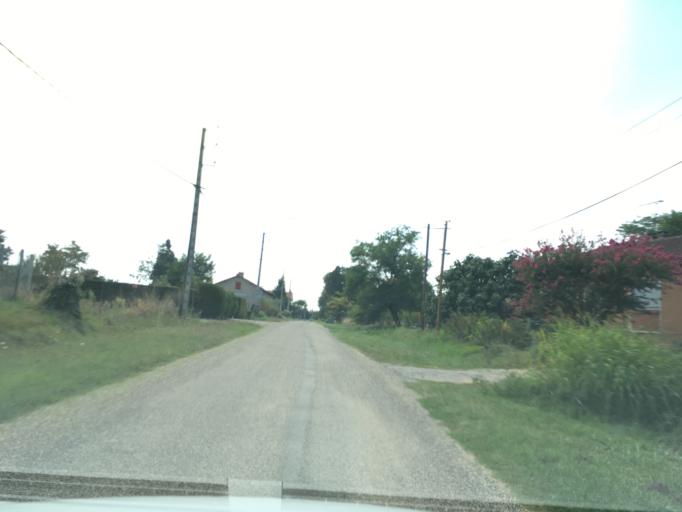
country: FR
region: Midi-Pyrenees
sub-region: Departement du Tarn-et-Garonne
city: Montbeton
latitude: 44.0154
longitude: 1.3155
